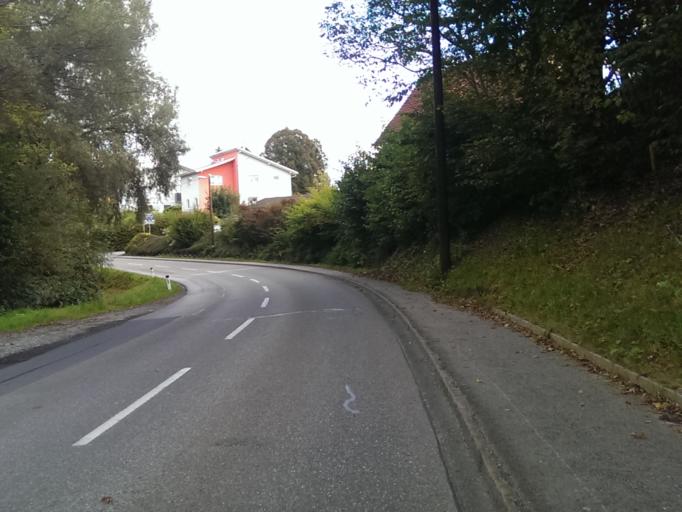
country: AT
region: Styria
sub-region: Politischer Bezirk Graz-Umgebung
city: Hart bei Graz
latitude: 47.0676
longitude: 15.5065
